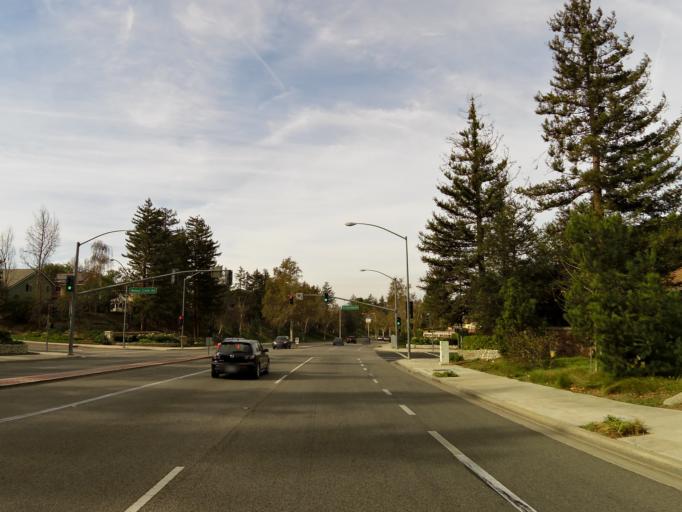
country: US
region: California
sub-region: Ventura County
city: Moorpark
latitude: 34.2636
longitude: -118.8861
